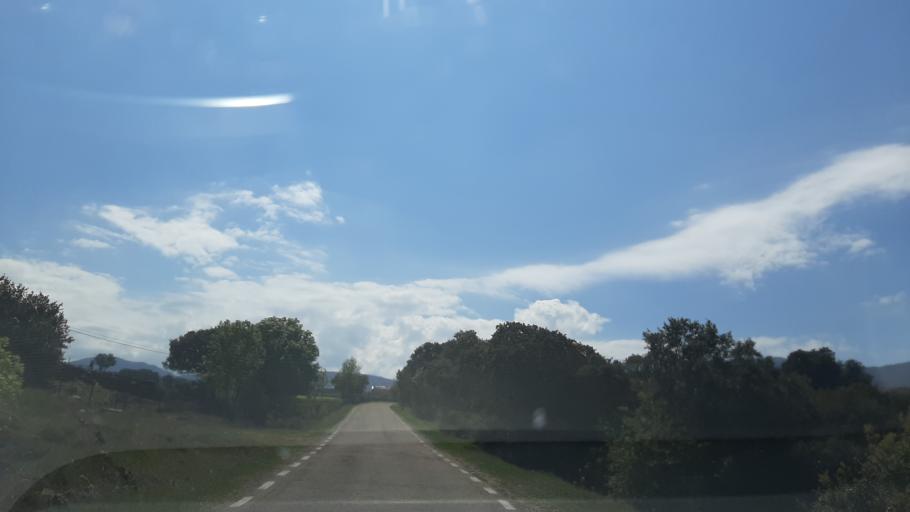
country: ES
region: Castille and Leon
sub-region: Provincia de Salamanca
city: Tejeda y Segoyuela
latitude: 40.6184
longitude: -6.0202
